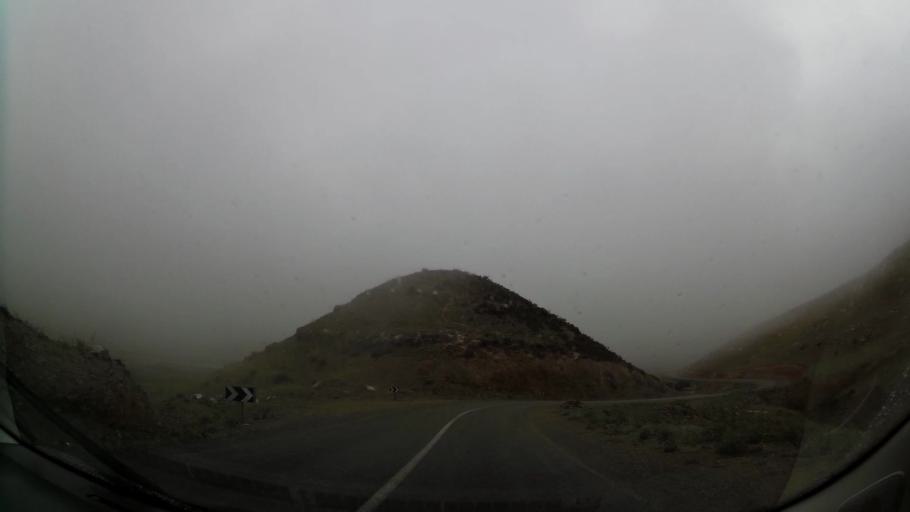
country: MA
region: Oriental
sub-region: Nador
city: Boudinar
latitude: 35.1065
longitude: -3.5657
